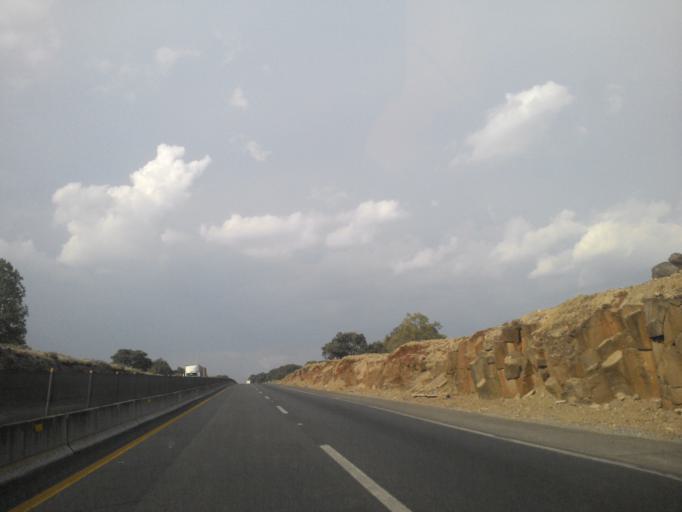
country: MX
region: Jalisco
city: Tepatitlan de Morelos
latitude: 20.8510
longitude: -102.7755
